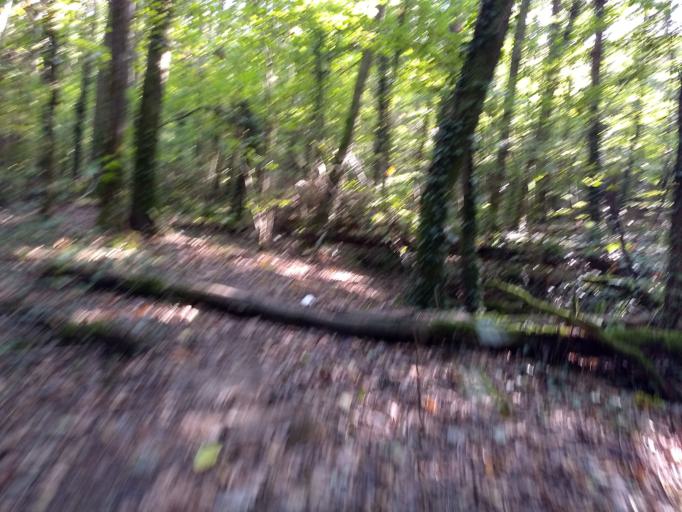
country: GB
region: England
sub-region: Isle of Wight
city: Newchurch
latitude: 50.7198
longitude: -1.2156
